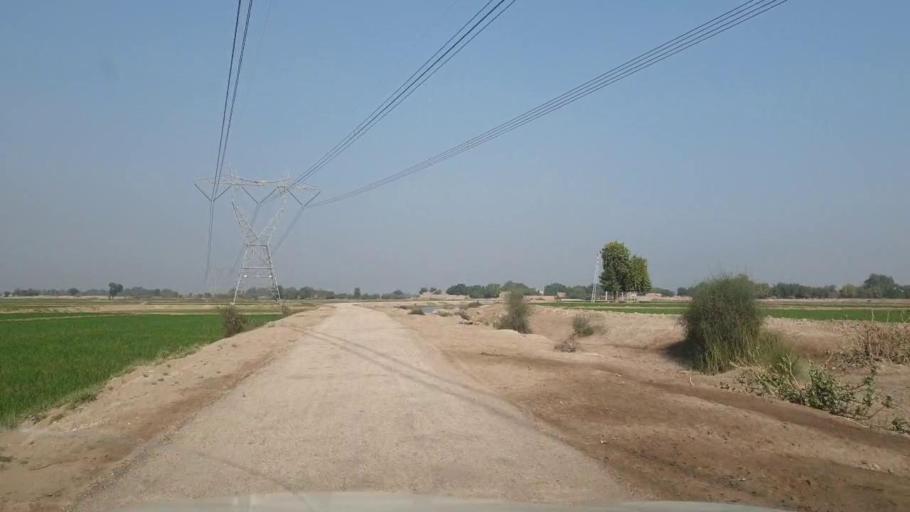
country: PK
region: Sindh
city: Bhan
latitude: 26.5447
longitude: 67.7485
